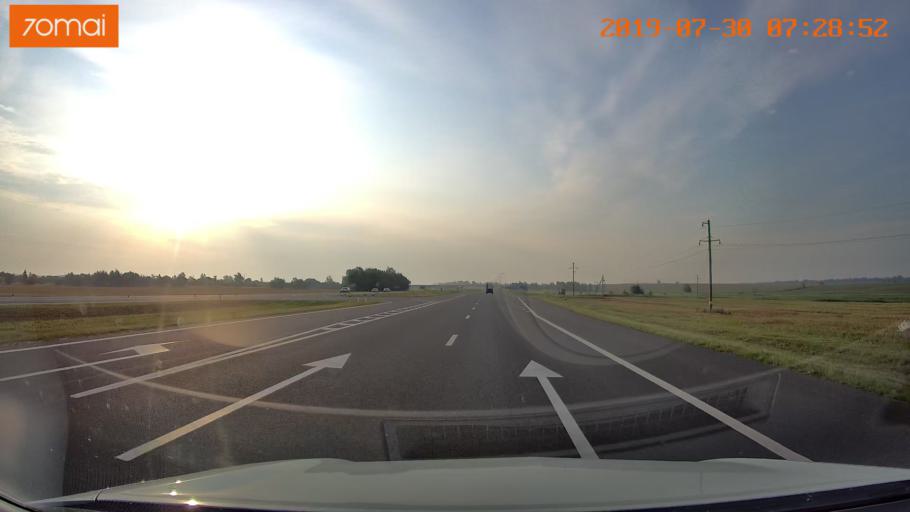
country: RU
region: Kaliningrad
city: Gvardeysk
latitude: 54.6753
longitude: 20.9241
